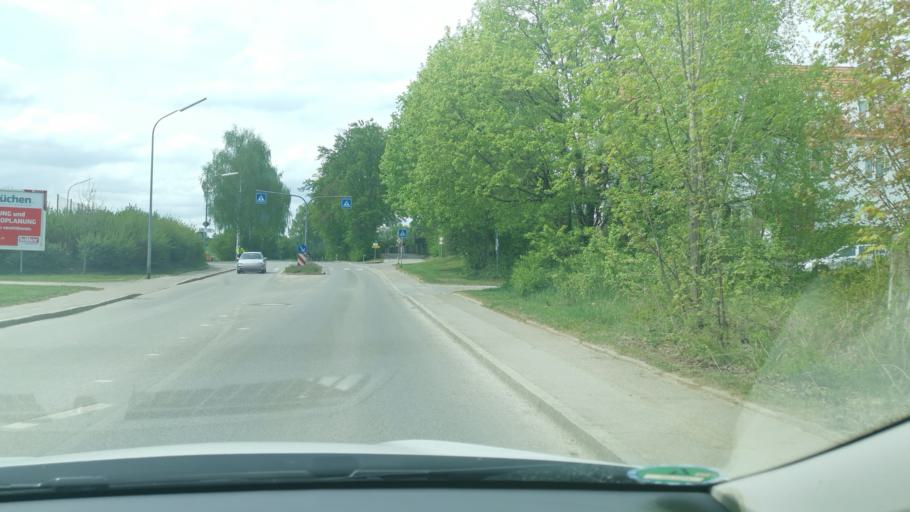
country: DE
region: Bavaria
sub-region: Upper Bavaria
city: Petershausen
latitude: 48.4101
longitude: 11.4660
